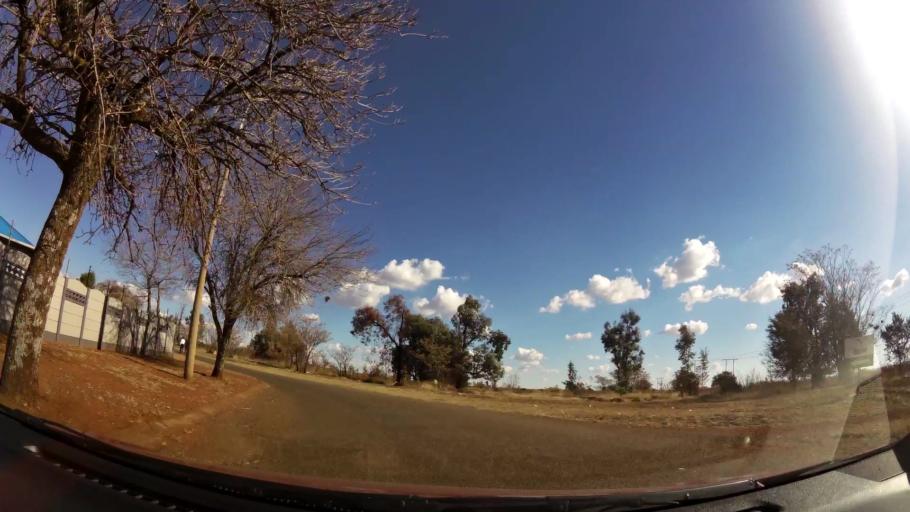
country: ZA
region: Gauteng
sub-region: West Rand District Municipality
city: Carletonville
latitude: -26.3615
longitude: 27.3612
